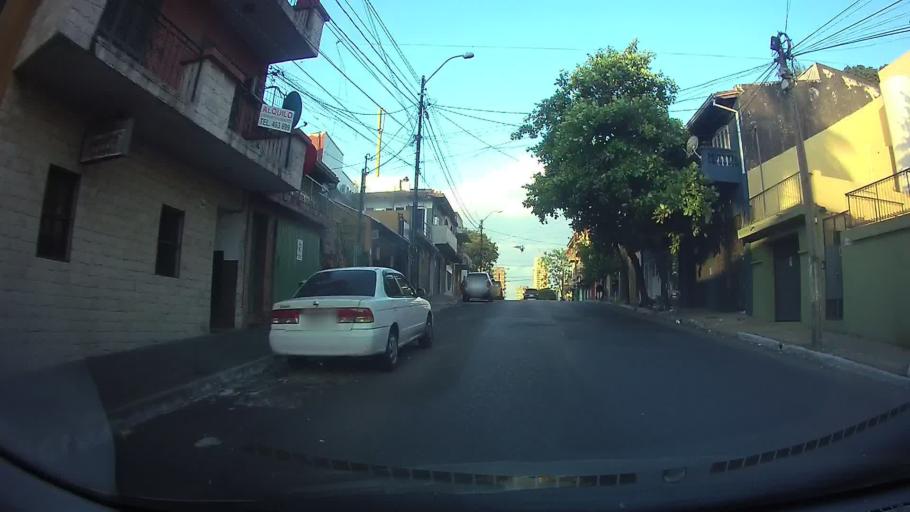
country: PY
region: Asuncion
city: Asuncion
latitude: -25.2937
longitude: -57.6283
